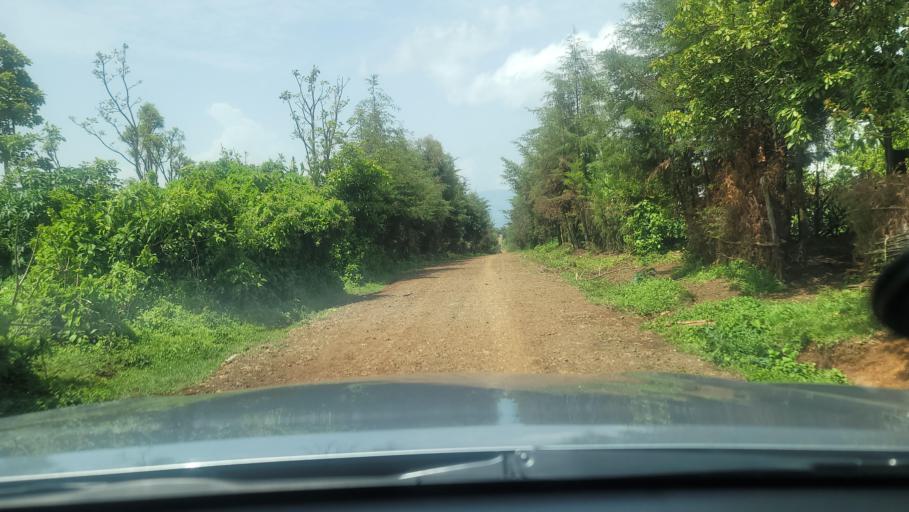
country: ET
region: Oromiya
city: Agaro
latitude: 7.8292
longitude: 36.4073
